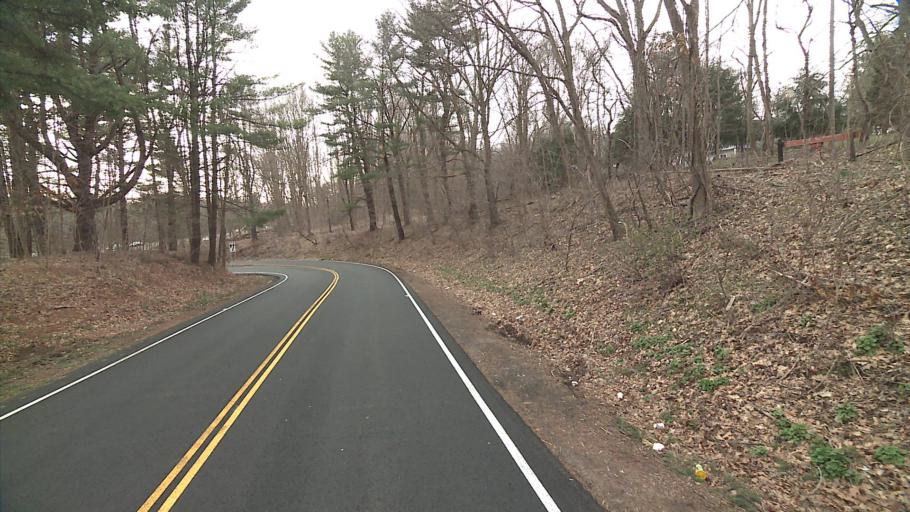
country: US
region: Connecticut
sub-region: New Haven County
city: Orange
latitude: 41.2873
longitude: -73.0427
